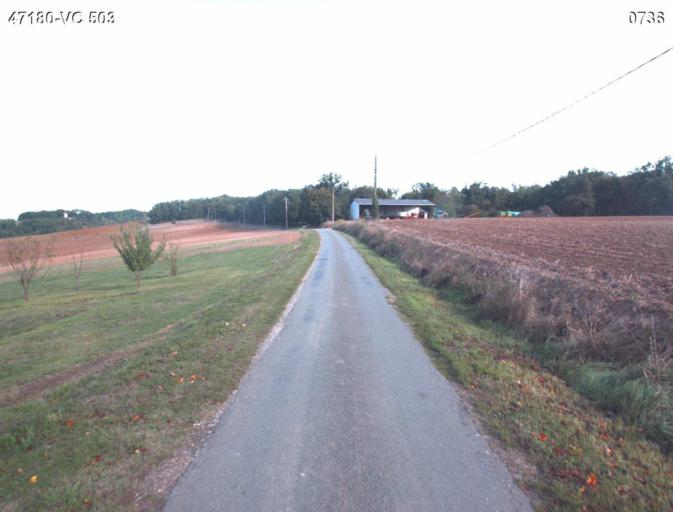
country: FR
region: Aquitaine
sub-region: Departement du Lot-et-Garonne
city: Sainte-Colombe-en-Bruilhois
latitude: 44.1772
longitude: 0.4321
